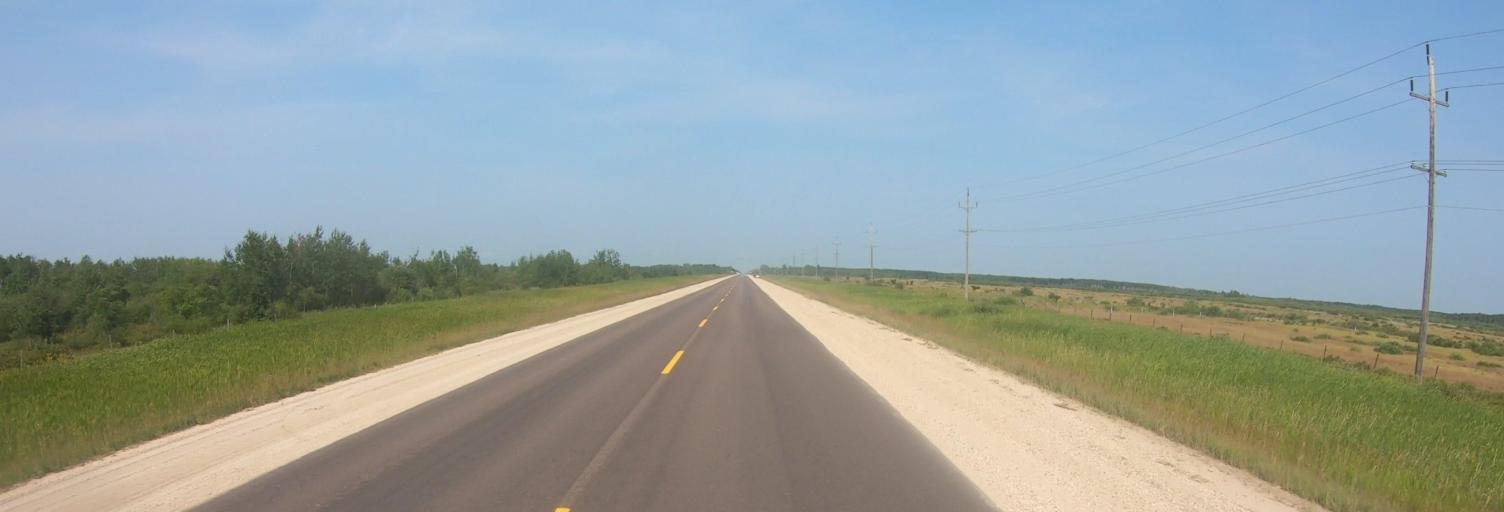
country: CA
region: Manitoba
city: La Broquerie
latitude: 49.2765
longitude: -96.4949
